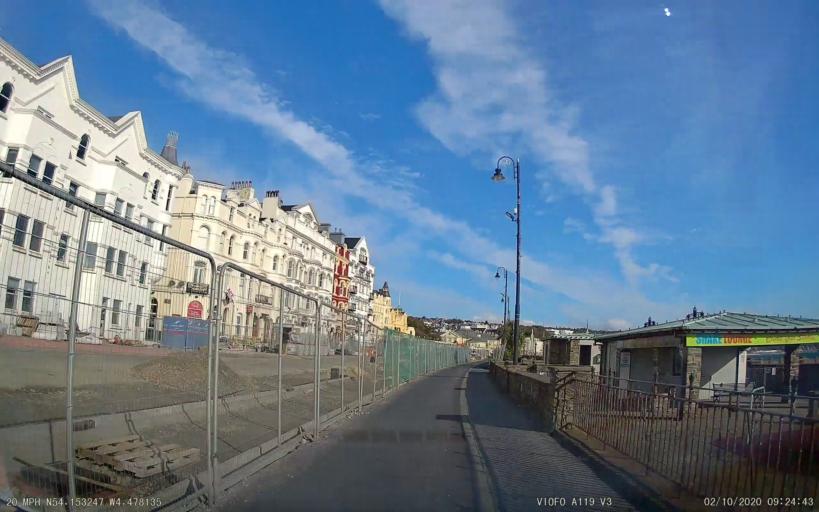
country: IM
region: Douglas
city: Douglas
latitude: 54.1533
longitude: -4.4782
